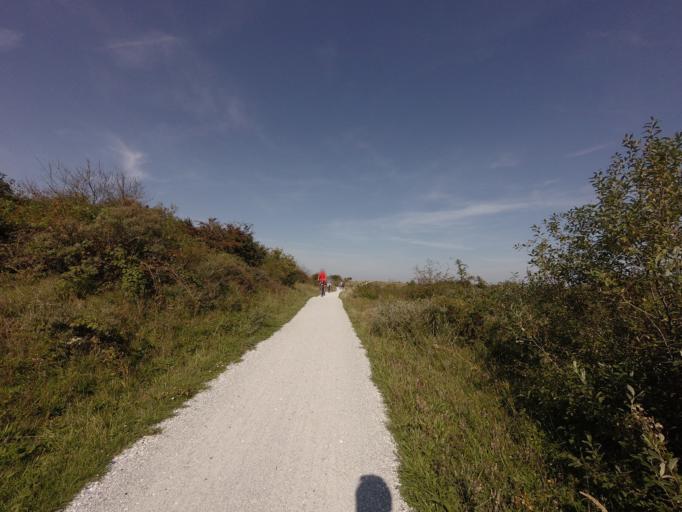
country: NL
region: Friesland
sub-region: Gemeente Schiermonnikoog
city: Schiermonnikoog
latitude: 53.4732
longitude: 6.1427
